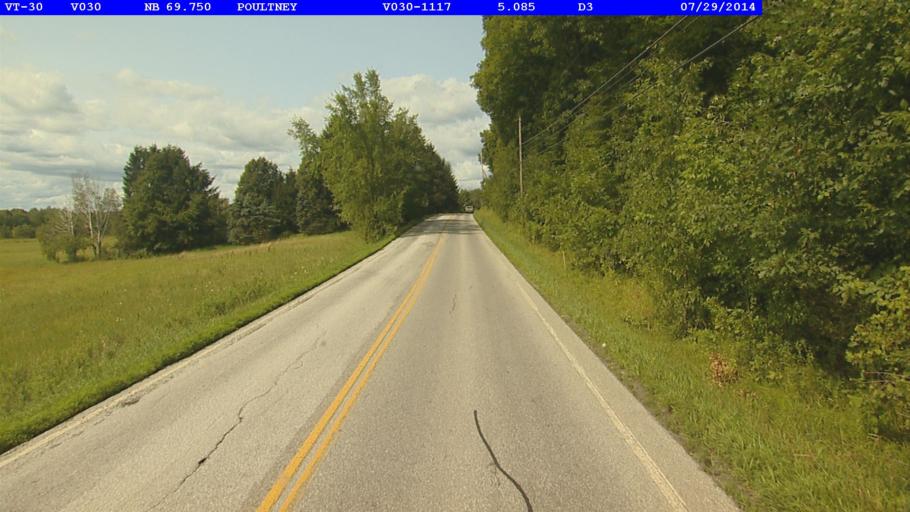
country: US
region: Vermont
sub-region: Rutland County
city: Poultney
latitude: 43.5244
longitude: -73.2317
